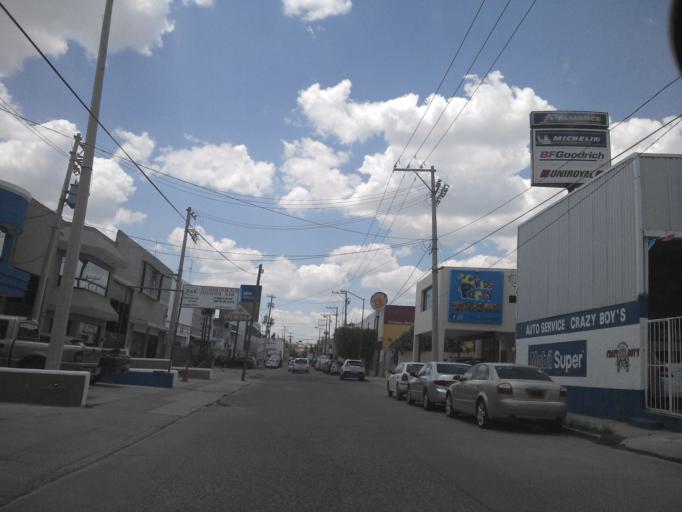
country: MX
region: Guanajuato
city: San Francisco del Rincon
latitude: 21.0274
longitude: -101.8578
